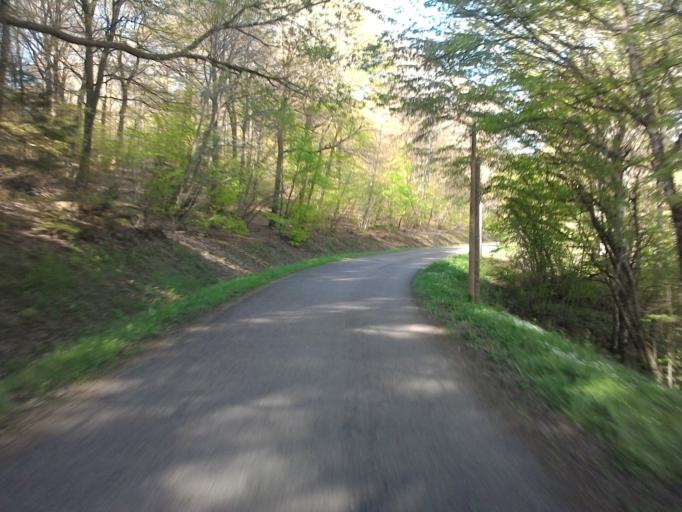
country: FR
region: Bourgogne
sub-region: Departement de l'Yonne
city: Avallon
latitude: 47.3504
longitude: 3.9455
